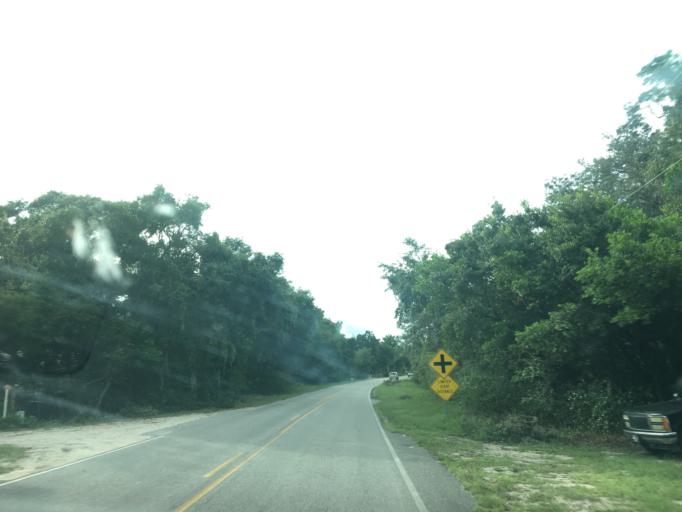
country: US
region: Florida
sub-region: Wakulla County
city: Crawfordville
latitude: 29.9116
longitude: -84.3644
